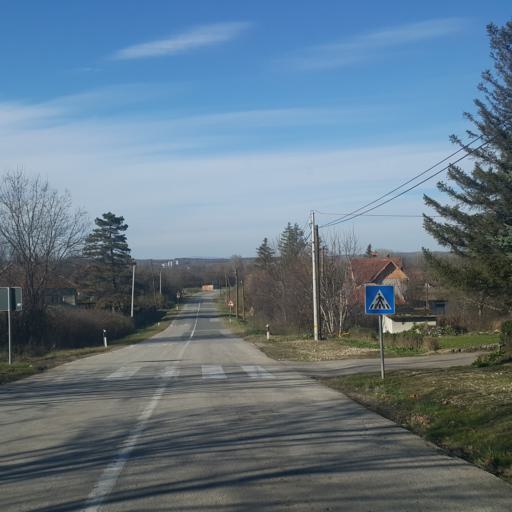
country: RS
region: Central Serbia
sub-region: Sumadijski Okrug
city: Raca
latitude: 44.2406
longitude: 20.8334
